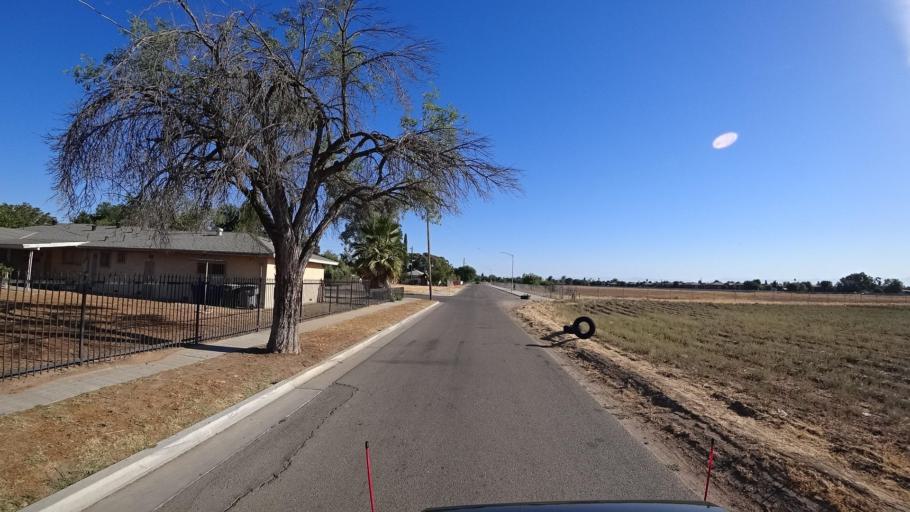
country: US
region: California
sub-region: Fresno County
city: Fresno
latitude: 36.7083
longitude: -119.7953
